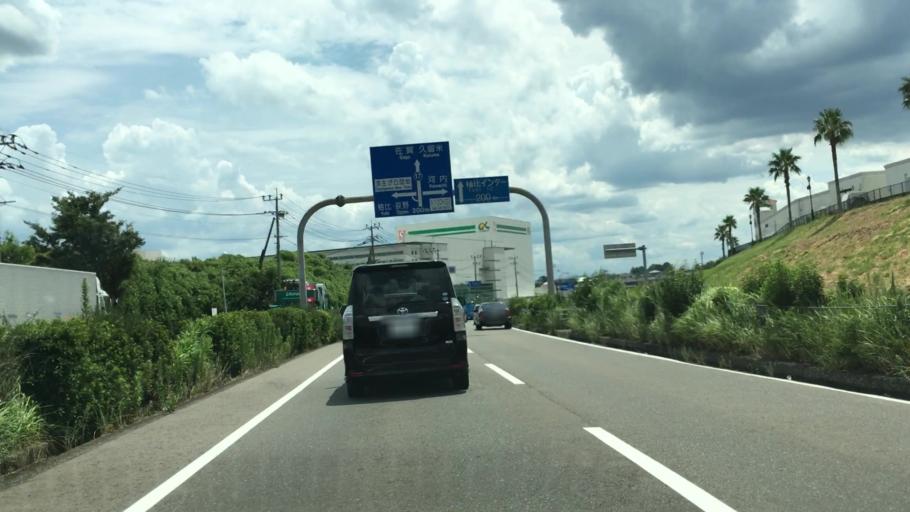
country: JP
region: Saga Prefecture
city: Tosu
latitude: 33.4066
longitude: 130.5129
